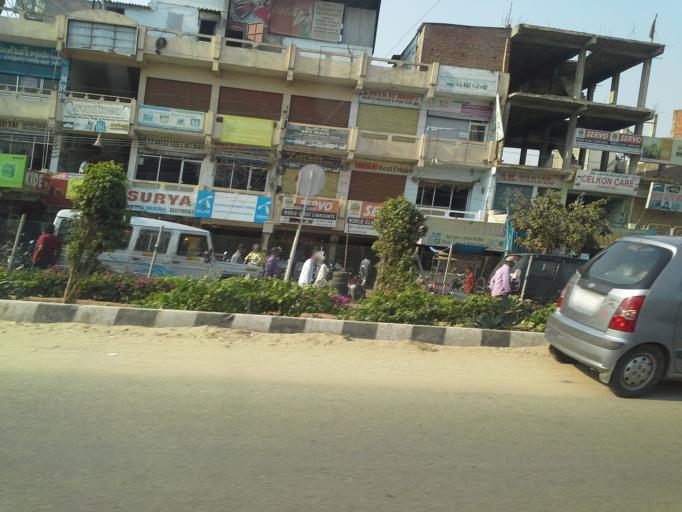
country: IN
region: Telangana
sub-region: Rangareddi
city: Balapur
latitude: 17.2631
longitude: 78.3890
